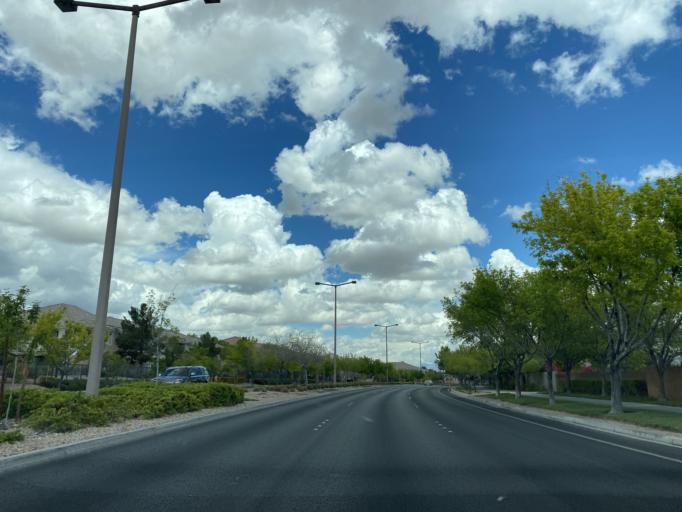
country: US
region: Nevada
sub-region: Clark County
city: Summerlin South
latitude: 36.1691
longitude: -115.3249
